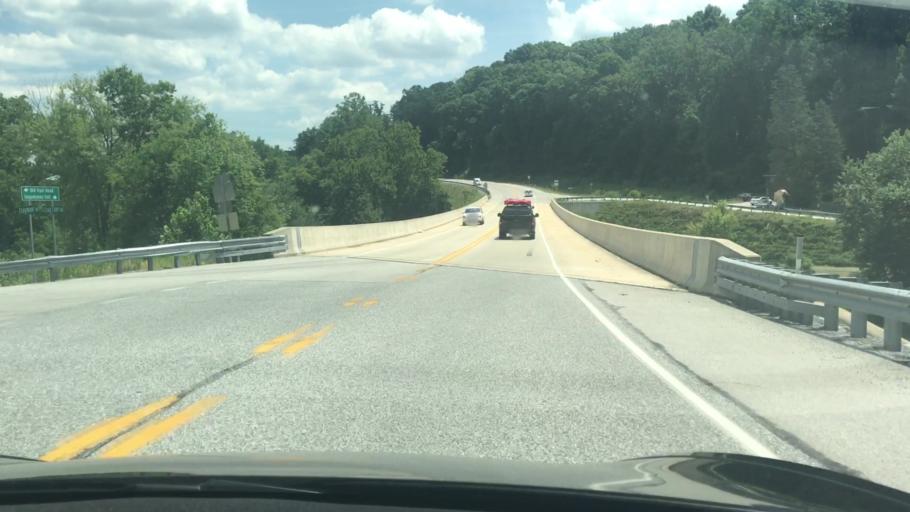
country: US
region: Pennsylvania
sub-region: York County
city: Manchester
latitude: 40.1007
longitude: -76.7643
